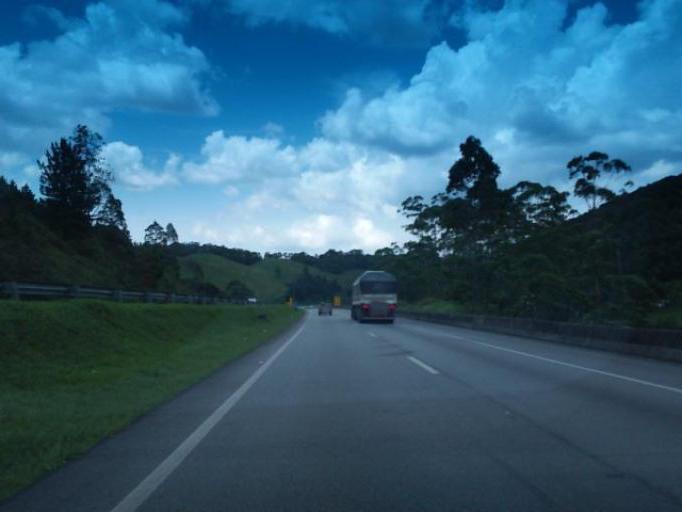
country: BR
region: Sao Paulo
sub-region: Juquitiba
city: Juquitiba
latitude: -23.9977
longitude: -47.1494
